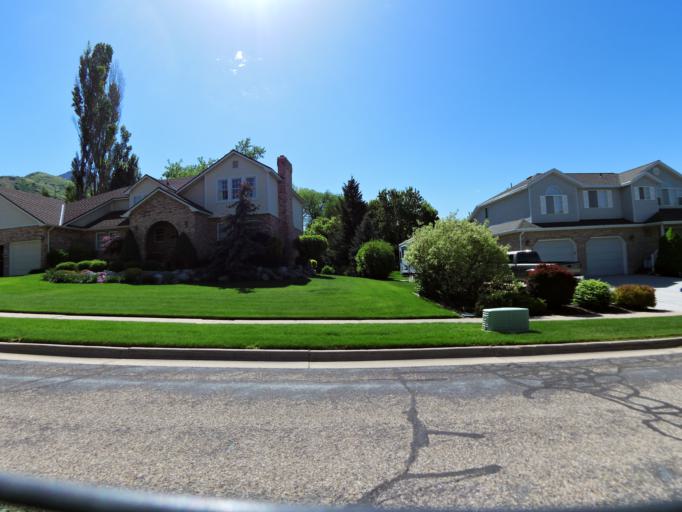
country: US
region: Utah
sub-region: Weber County
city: Uintah
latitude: 41.1694
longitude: -111.9320
